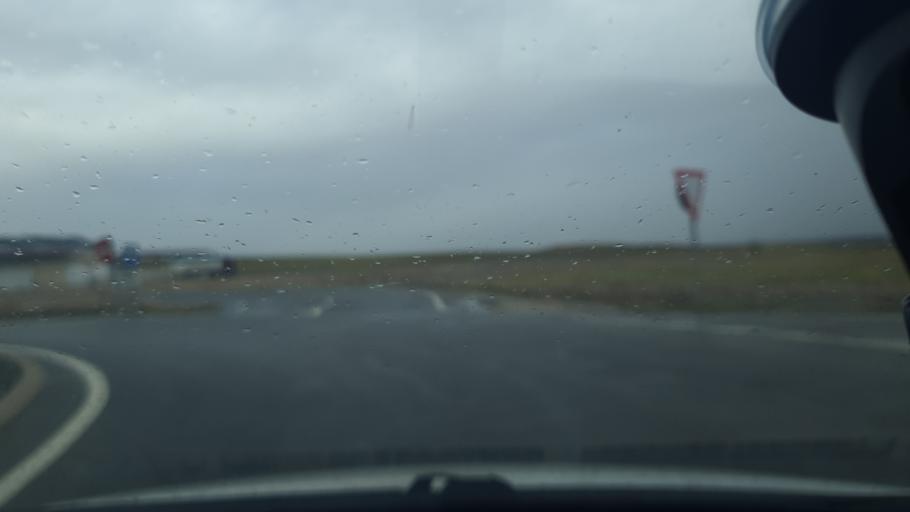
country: ES
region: Castille and Leon
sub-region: Provincia de Segovia
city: Carbonero el Mayor
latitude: 41.1122
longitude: -4.2523
